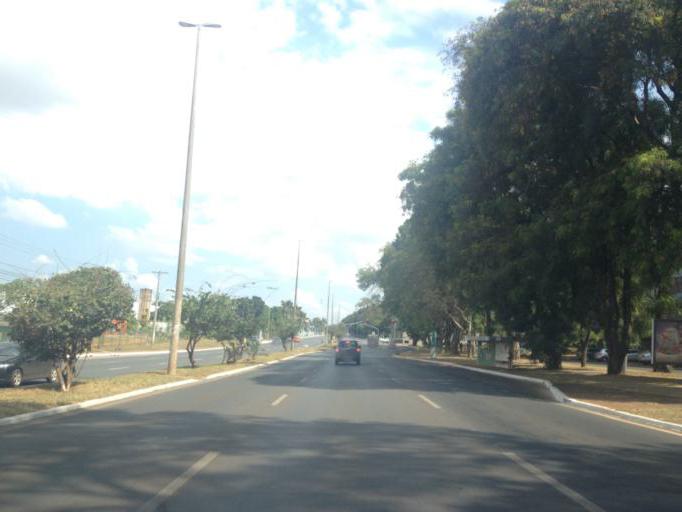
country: BR
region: Federal District
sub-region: Brasilia
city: Brasilia
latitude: -15.8345
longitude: -47.9140
